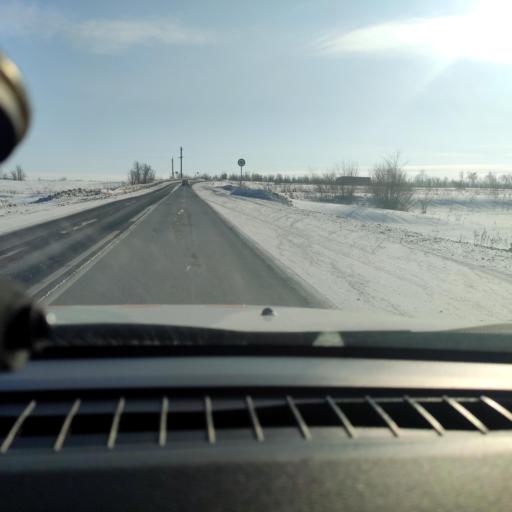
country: RU
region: Samara
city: Smyshlyayevka
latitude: 53.1570
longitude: 50.4568
